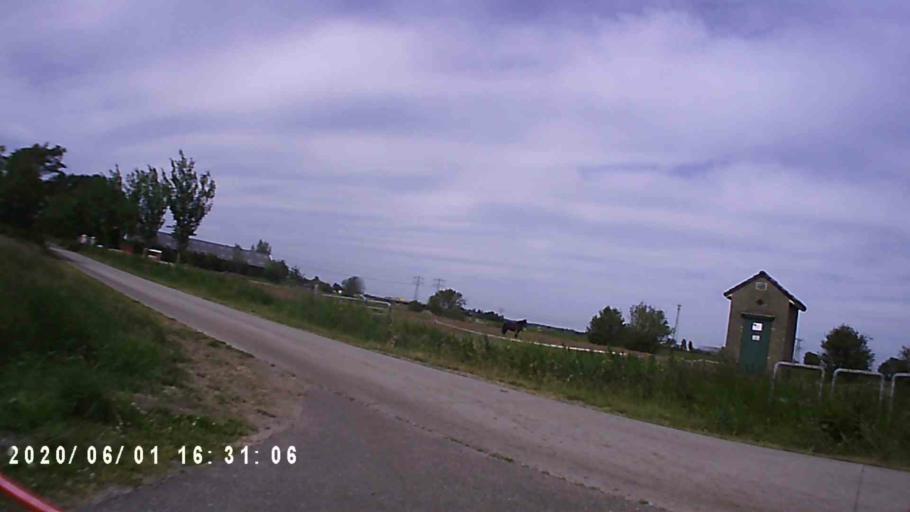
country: NL
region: Friesland
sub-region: Gemeente Leeuwarden
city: Camminghaburen
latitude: 53.1857
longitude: 5.8663
